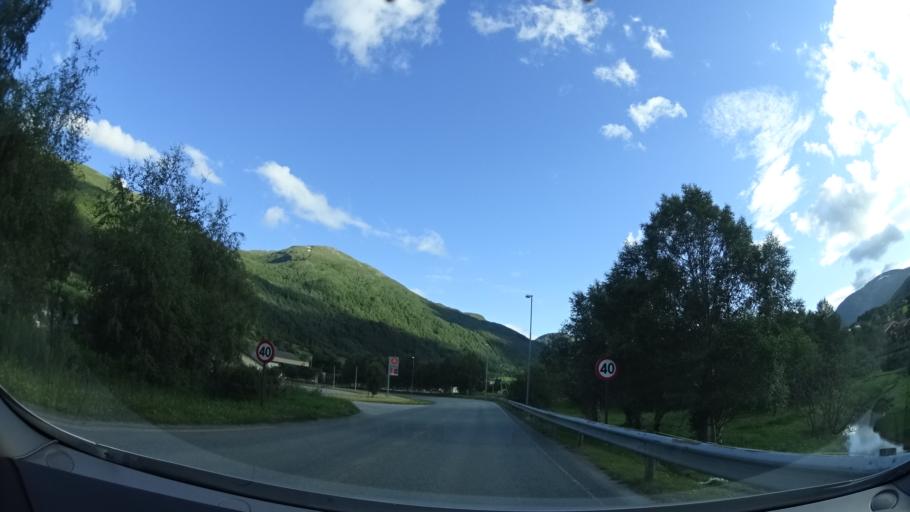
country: NO
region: More og Romsdal
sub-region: Gjemnes
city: Batnfjordsora
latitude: 62.8957
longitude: 7.6767
